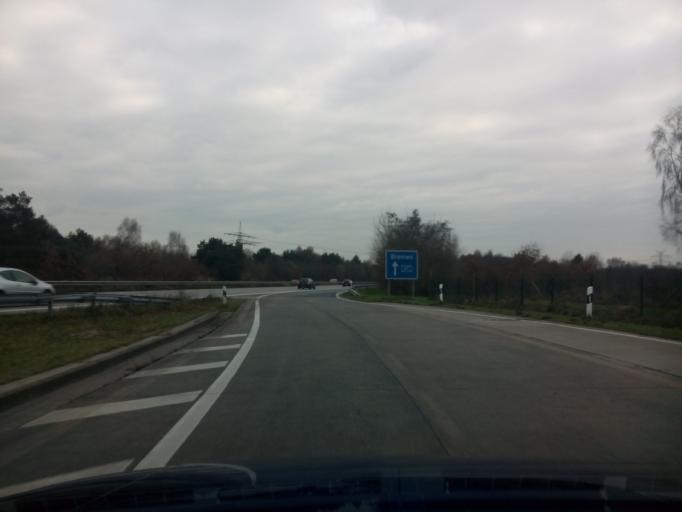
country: DE
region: Lower Saxony
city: Langen
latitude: 53.6077
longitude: 8.6577
